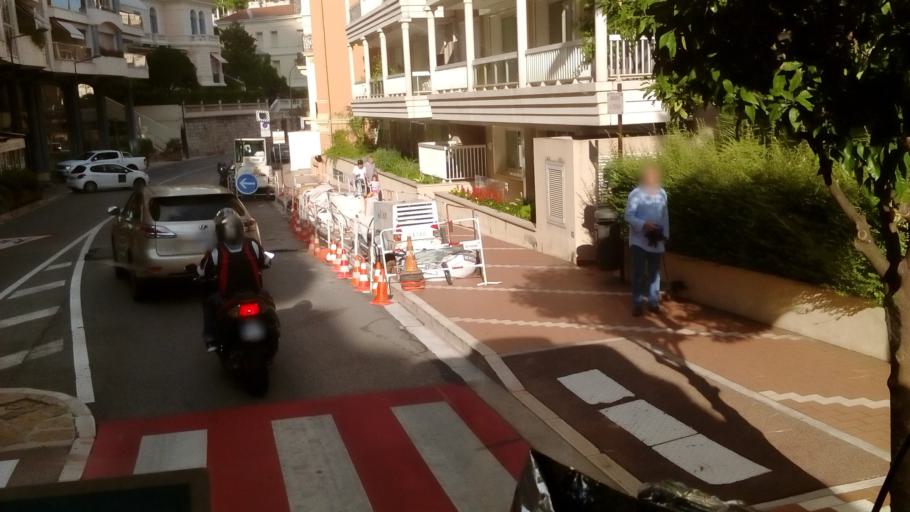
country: MC
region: Commune de Monaco
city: Saint-Roman
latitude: 43.7486
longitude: 7.4337
